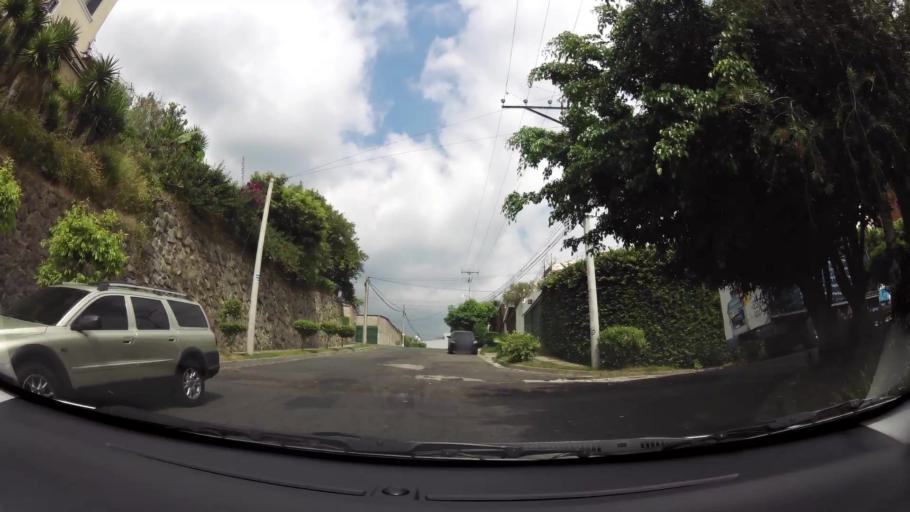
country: SV
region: La Libertad
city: Santa Tecla
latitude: 13.7116
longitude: -89.2517
